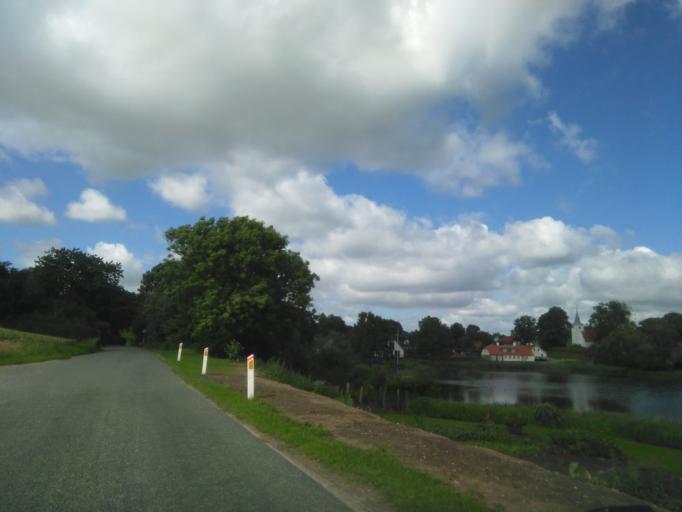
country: DK
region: Central Jutland
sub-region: Syddjurs Kommune
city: Ronde
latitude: 56.2301
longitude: 10.5218
